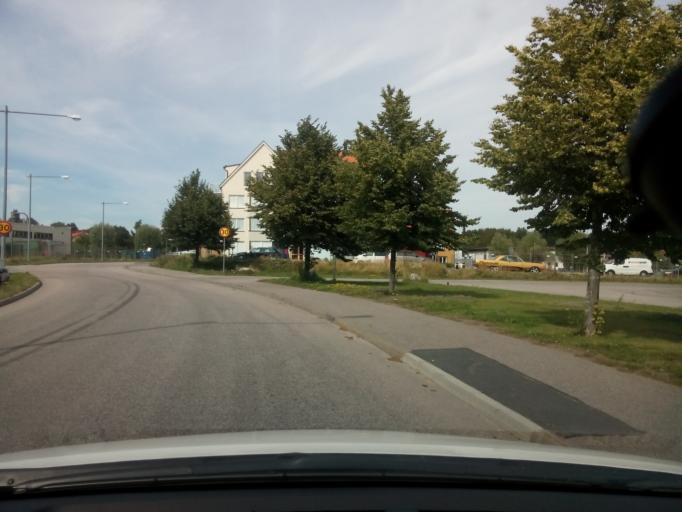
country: SE
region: Soedermanland
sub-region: Nykopings Kommun
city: Nykoping
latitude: 58.7486
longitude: 17.0284
